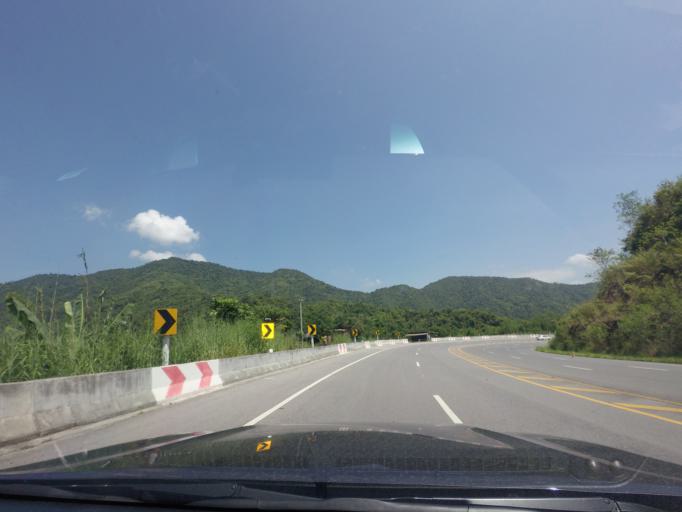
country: TH
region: Phetchabun
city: Lom Sak
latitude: 16.7729
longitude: 101.1242
